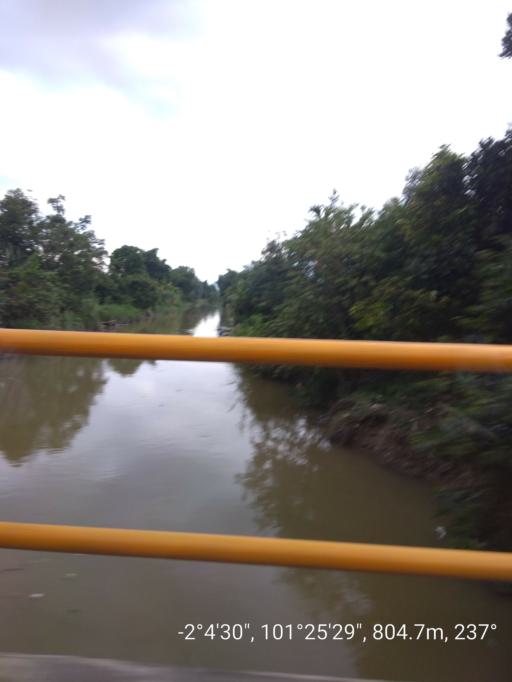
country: ID
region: Jambi
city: Sungai Penuh
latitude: -2.0751
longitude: 101.4248
